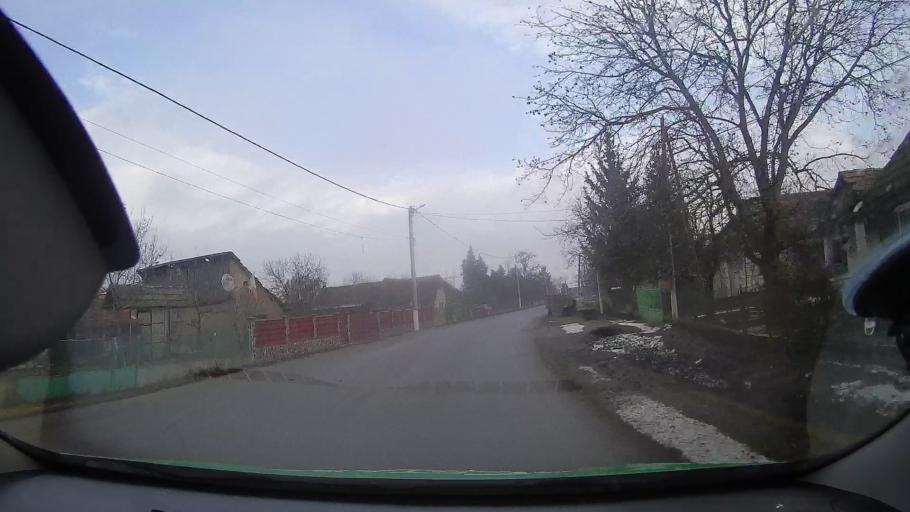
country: RO
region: Alba
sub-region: Comuna Noslac
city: Noslac
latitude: 46.4200
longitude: 23.9801
